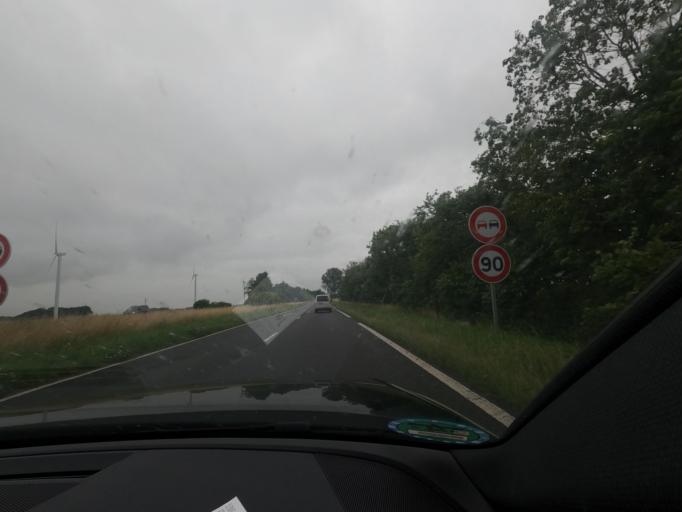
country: FR
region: Picardie
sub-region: Departement de la Somme
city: Roye
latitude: 49.7278
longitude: 2.7184
